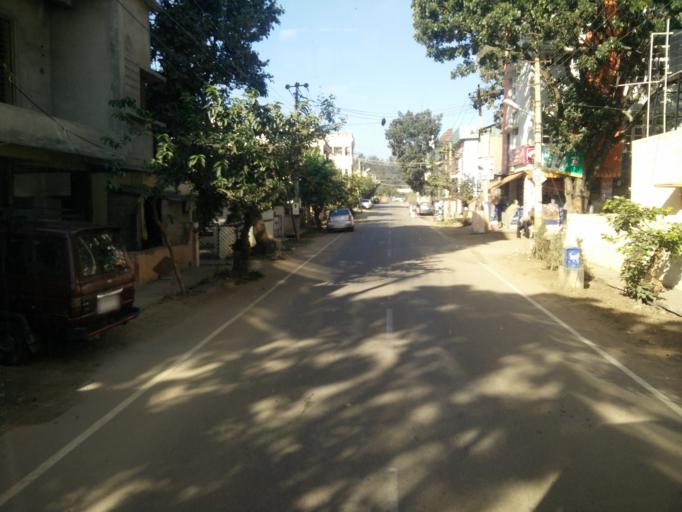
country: IN
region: Karnataka
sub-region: Bangalore Urban
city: Yelahanka
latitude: 13.0966
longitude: 77.5975
